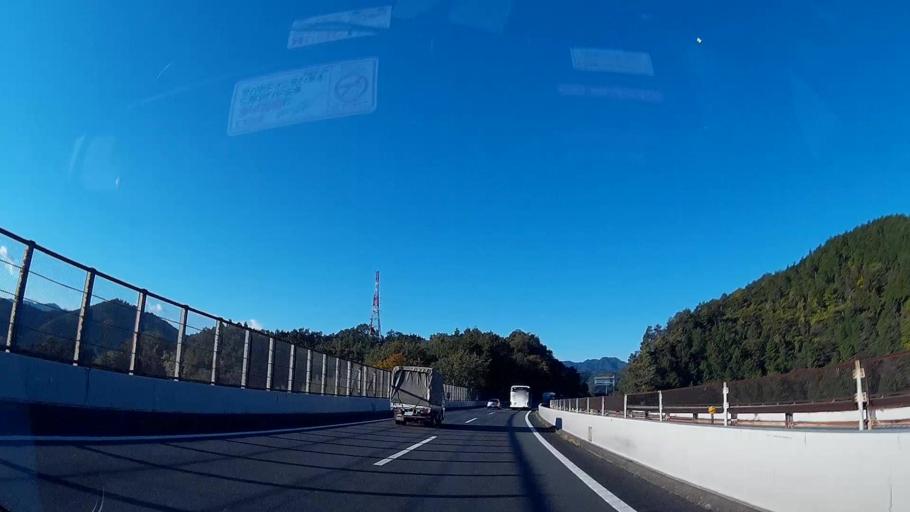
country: JP
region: Yamanashi
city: Uenohara
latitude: 35.6166
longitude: 139.1630
